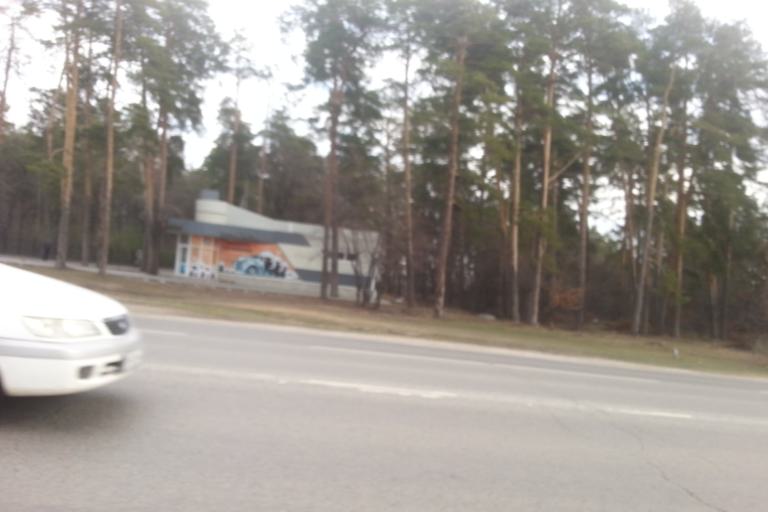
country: RU
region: Altai Krai
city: Zaton
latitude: 53.2803
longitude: 83.7485
